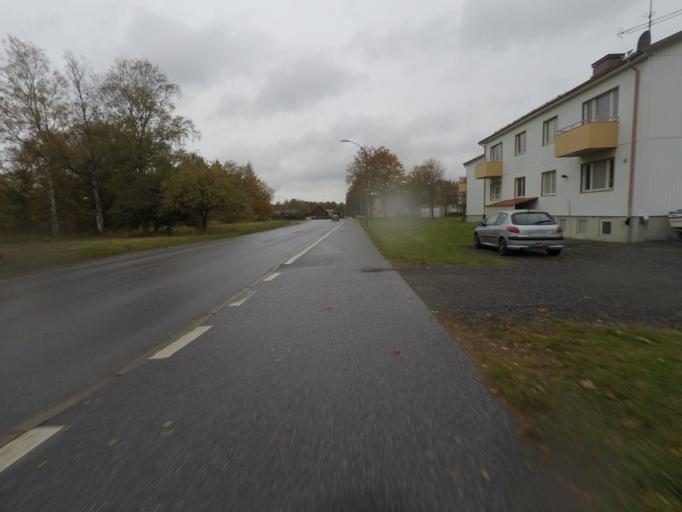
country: SE
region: OErebro
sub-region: Karlskoga Kommun
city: Karlskoga
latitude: 59.3275
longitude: 14.4988
